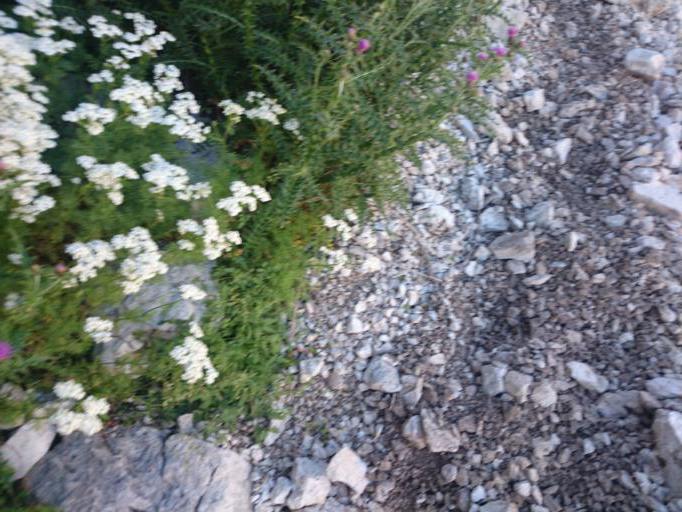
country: AL
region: Elbasan
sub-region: Rrethi i Gramshit
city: Kushove
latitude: 40.7141
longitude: 20.1501
